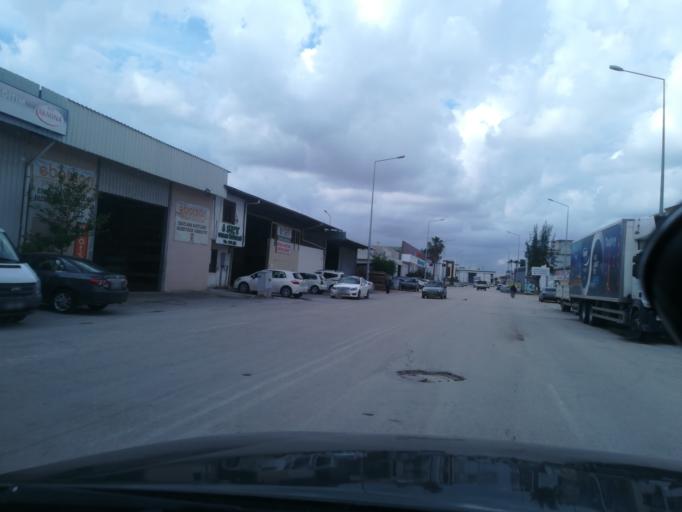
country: TR
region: Adana
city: Yuregir
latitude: 36.9779
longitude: 35.3928
